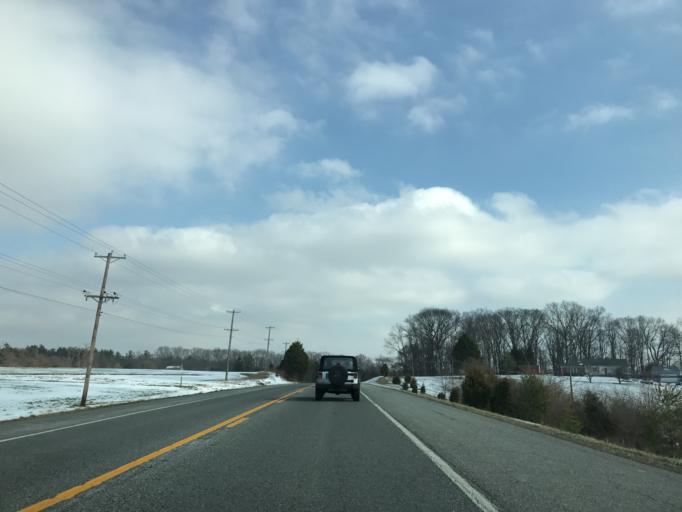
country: US
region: Pennsylvania
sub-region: York County
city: Susquehanna Trails
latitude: 39.6872
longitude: -76.2981
